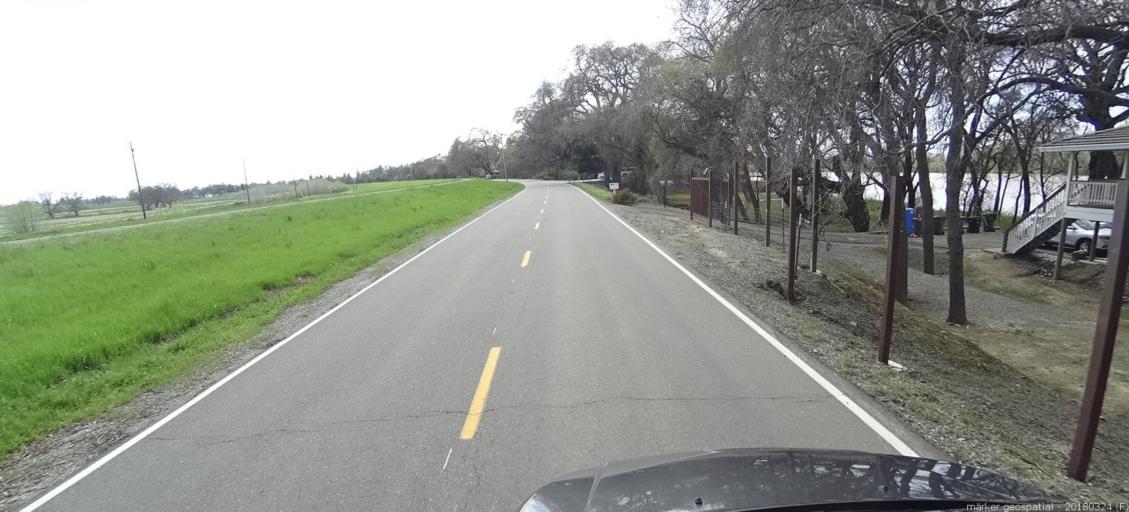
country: US
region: California
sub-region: Yolo County
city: Woodland
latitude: 38.6988
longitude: -121.6270
